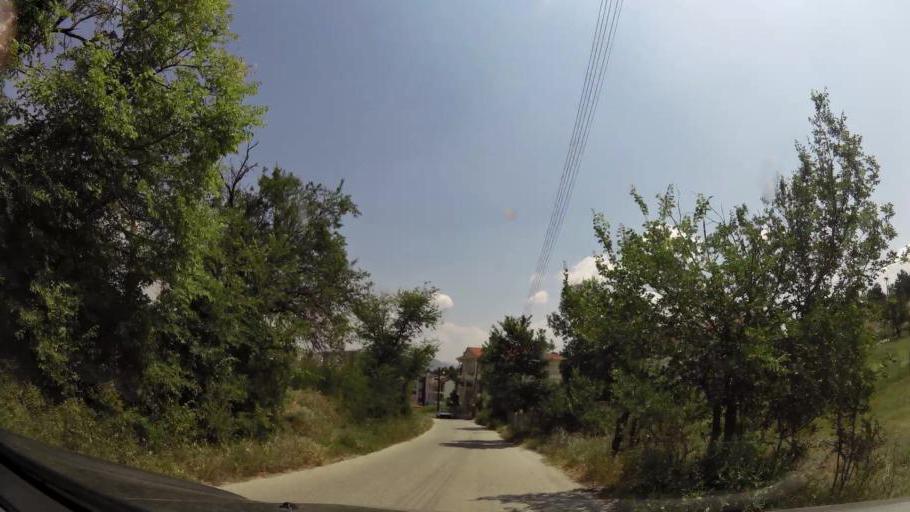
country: GR
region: West Macedonia
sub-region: Nomos Kozanis
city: Kozani
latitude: 40.2976
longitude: 21.7767
